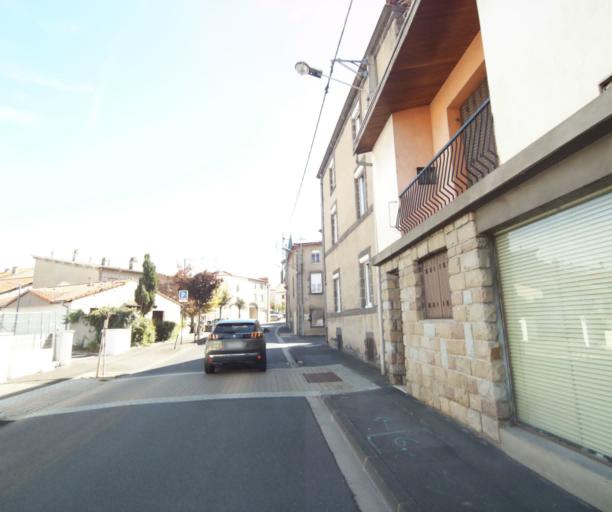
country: FR
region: Auvergne
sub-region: Departement du Puy-de-Dome
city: Cournon-d'Auvergne
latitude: 45.7710
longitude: 3.1964
